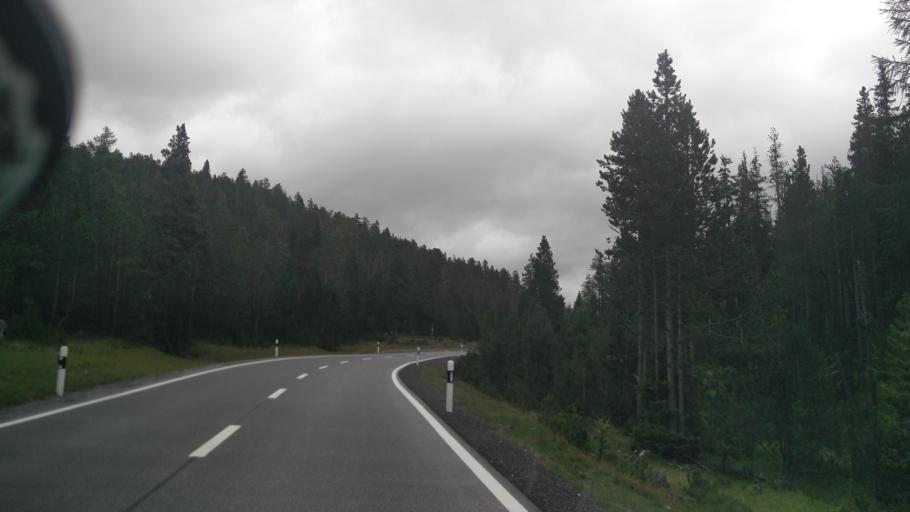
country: CH
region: Grisons
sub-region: Inn District
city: Zernez
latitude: 46.6818
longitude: 10.1570
